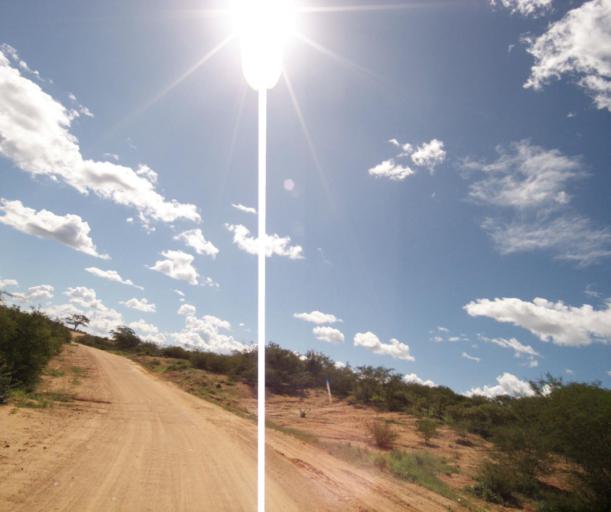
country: BR
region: Bahia
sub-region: Pocoes
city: Pocoes
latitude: -14.2487
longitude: -40.7459
